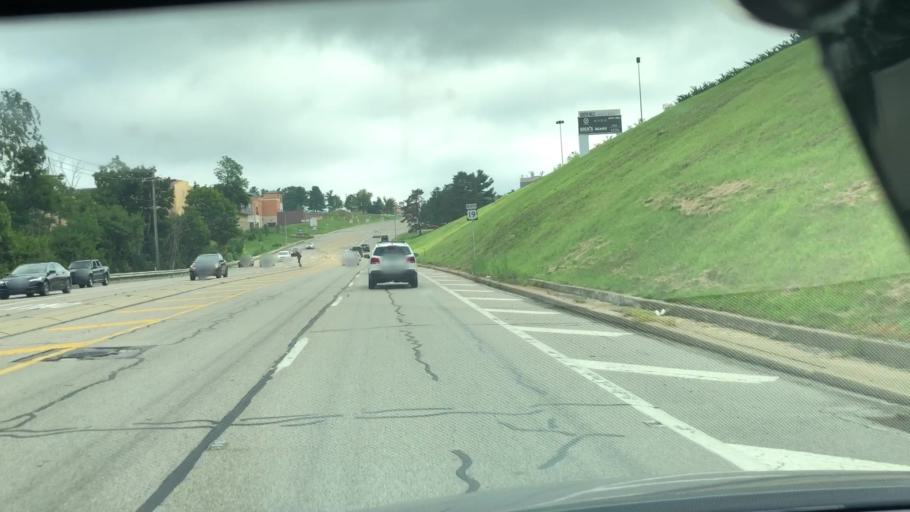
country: US
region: Pennsylvania
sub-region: Allegheny County
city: Mount Lebanon
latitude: 40.3440
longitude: -80.0594
